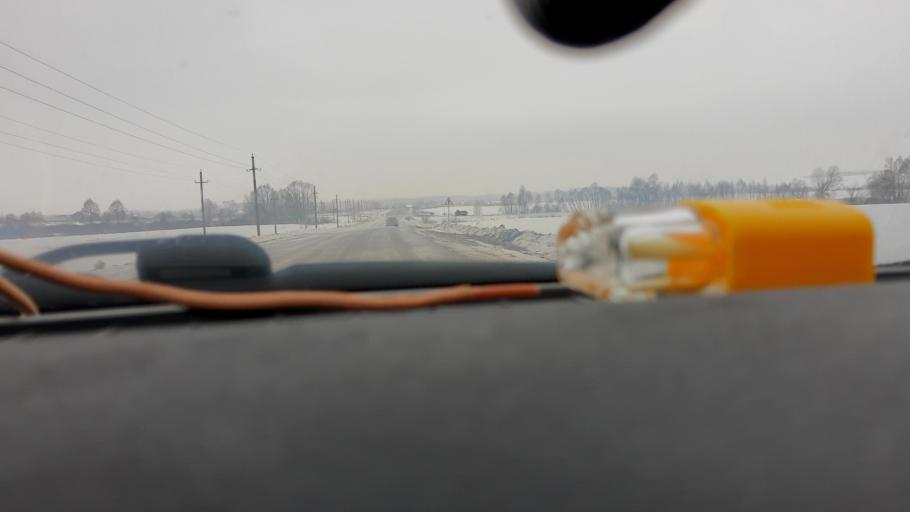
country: RU
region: Bashkortostan
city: Ulukulevo
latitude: 54.5193
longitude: 56.4202
